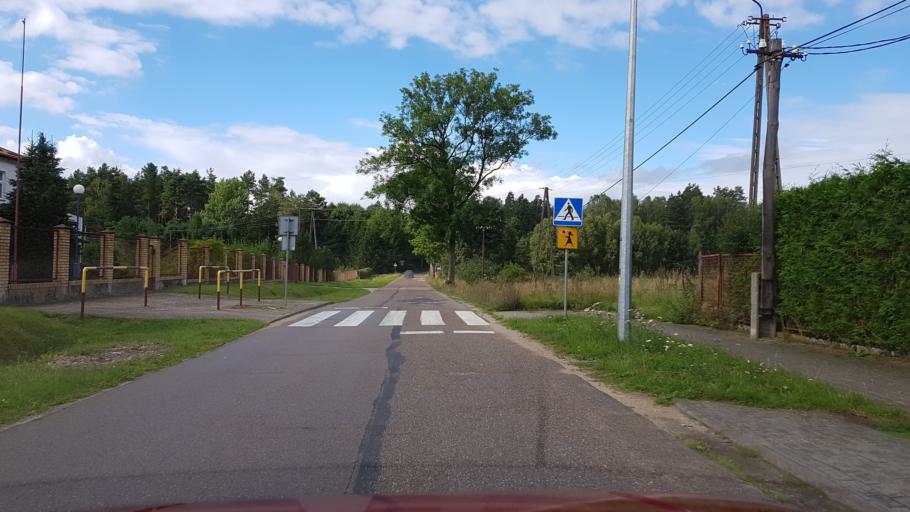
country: PL
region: West Pomeranian Voivodeship
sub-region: Powiat bialogardzki
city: Tychowo
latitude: 54.0156
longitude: 16.3949
